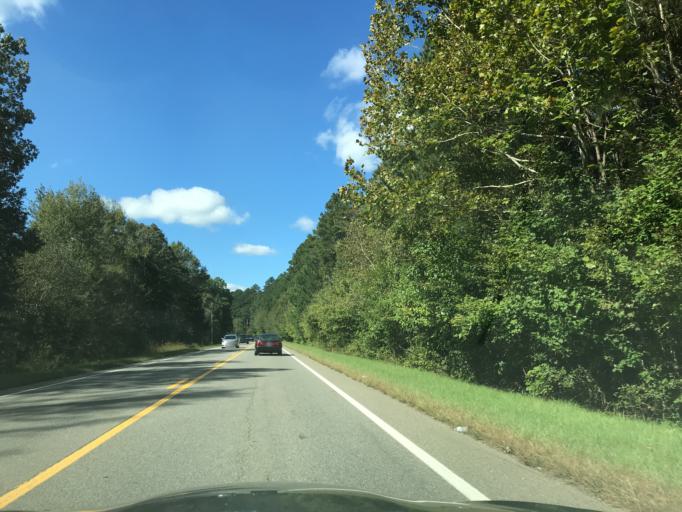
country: US
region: North Carolina
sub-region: Durham County
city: Gorman
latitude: 35.9811
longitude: -78.7393
